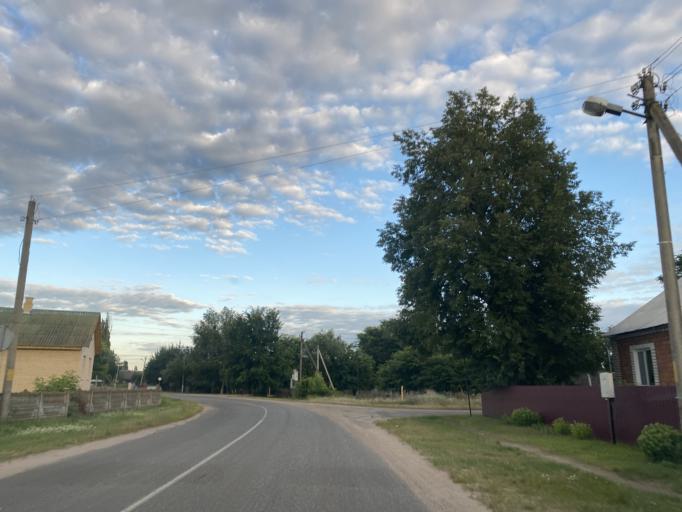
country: BY
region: Brest
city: Ivanava
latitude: 52.3494
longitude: 25.6099
